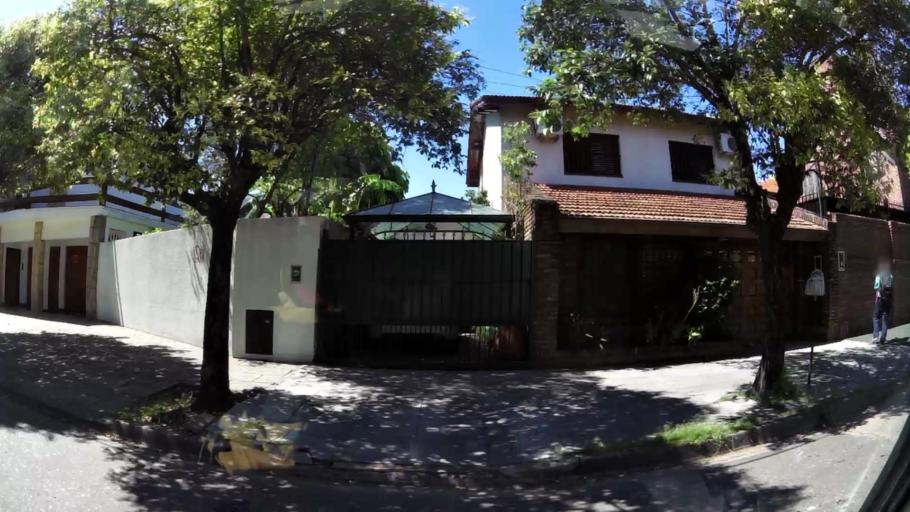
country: AR
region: Buenos Aires
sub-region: Partido de Vicente Lopez
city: Olivos
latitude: -34.5195
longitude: -58.4953
